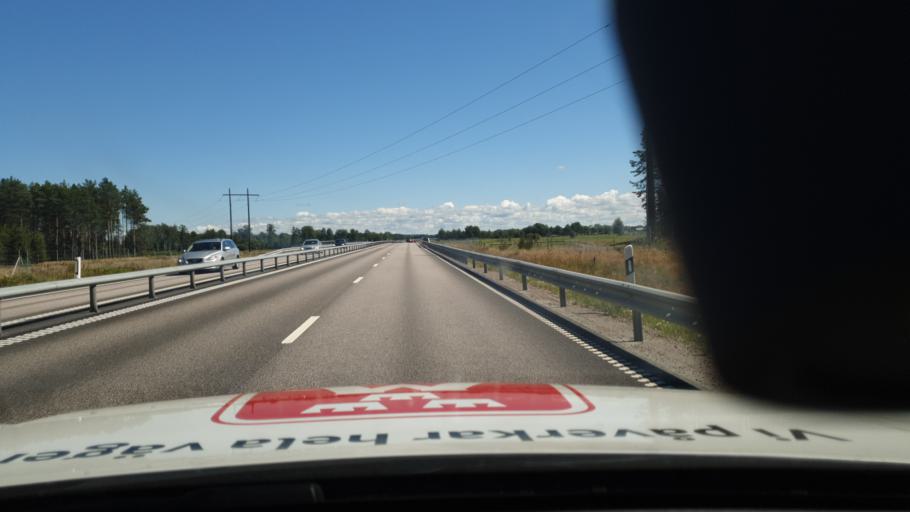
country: SE
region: Vaestra Goetaland
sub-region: Lidkopings Kommun
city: Vinninga
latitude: 58.4794
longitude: 13.2137
